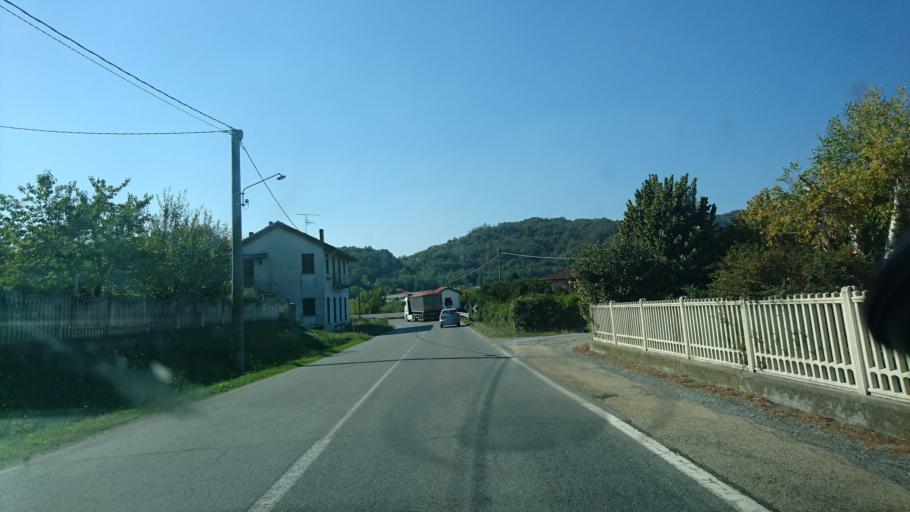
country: IT
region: Piedmont
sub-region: Provincia di Alessandria
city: Spigno Monferrato
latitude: 44.5404
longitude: 8.3258
